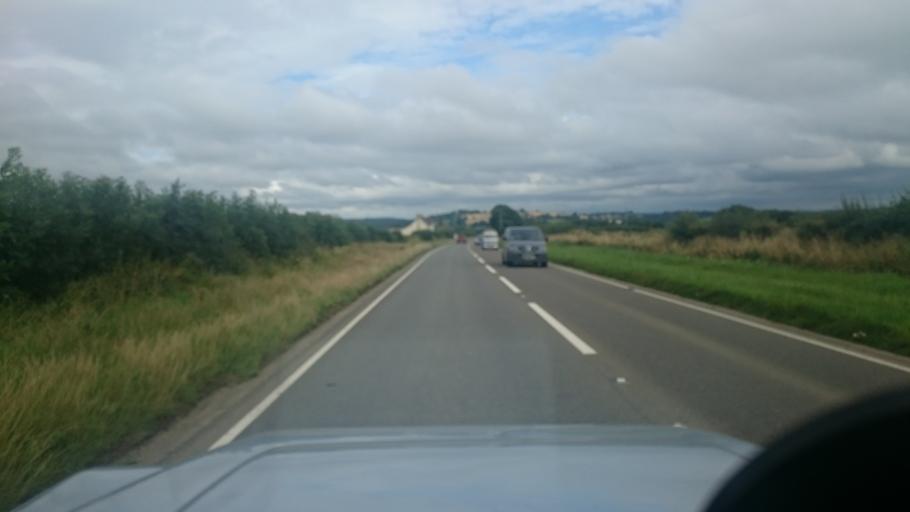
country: GB
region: Wales
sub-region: Pembrokeshire
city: Hook
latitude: 51.8055
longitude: -4.9206
